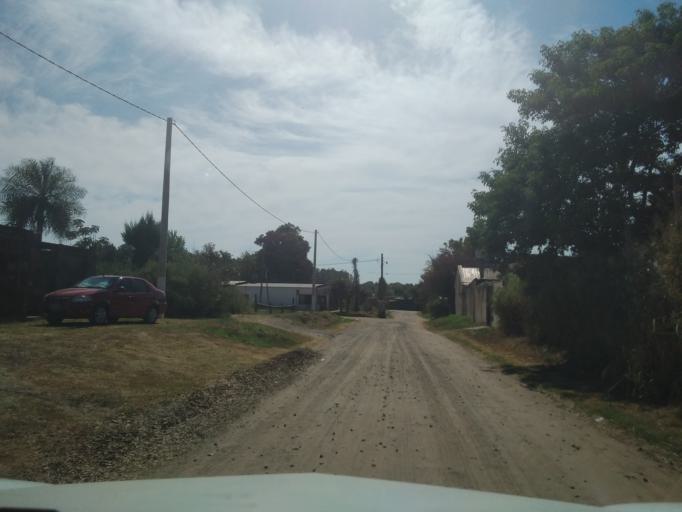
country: AR
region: Corrientes
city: Corrientes
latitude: -27.5108
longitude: -58.8057
